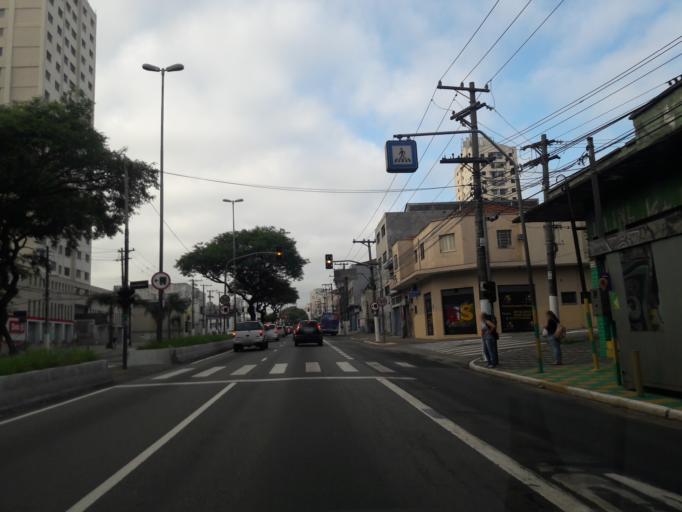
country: BR
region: Sao Paulo
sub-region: Sao Caetano Do Sul
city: Sao Caetano do Sul
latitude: -23.6127
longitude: -46.6007
